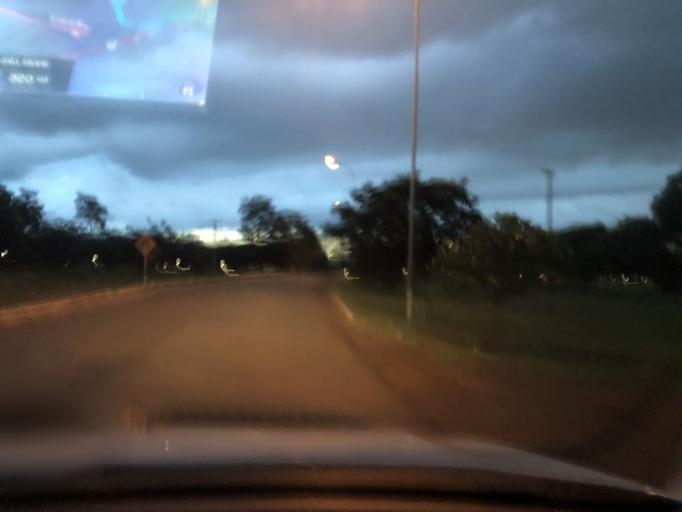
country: BR
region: Federal District
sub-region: Brasilia
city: Brasilia
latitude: -15.8350
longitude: -47.9302
